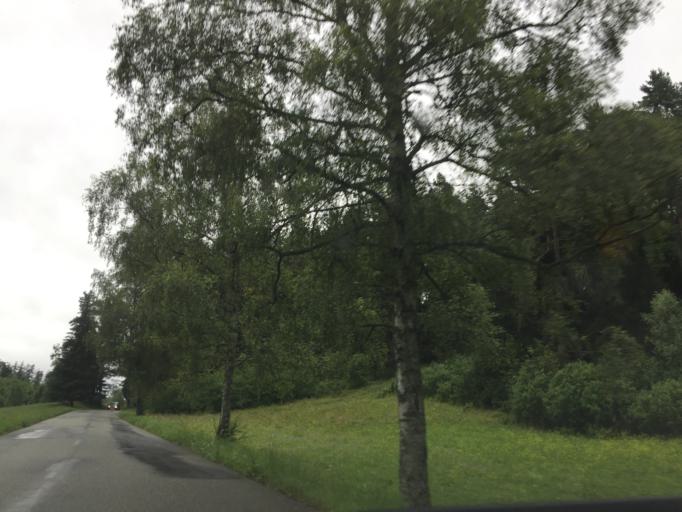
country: CZ
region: South Moravian
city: Ostrov u Macochy
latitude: 49.3874
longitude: 16.7685
